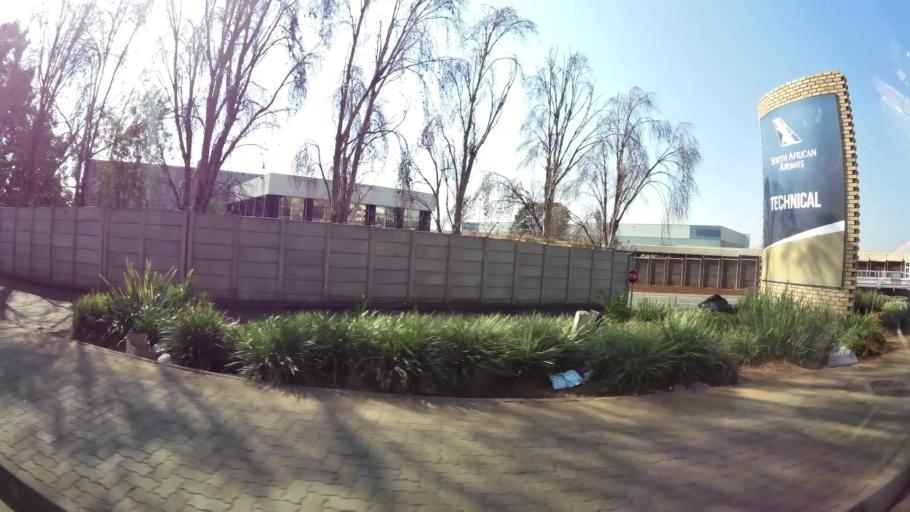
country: ZA
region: Gauteng
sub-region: Ekurhuleni Metropolitan Municipality
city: Boksburg
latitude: -26.1437
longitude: 28.2236
